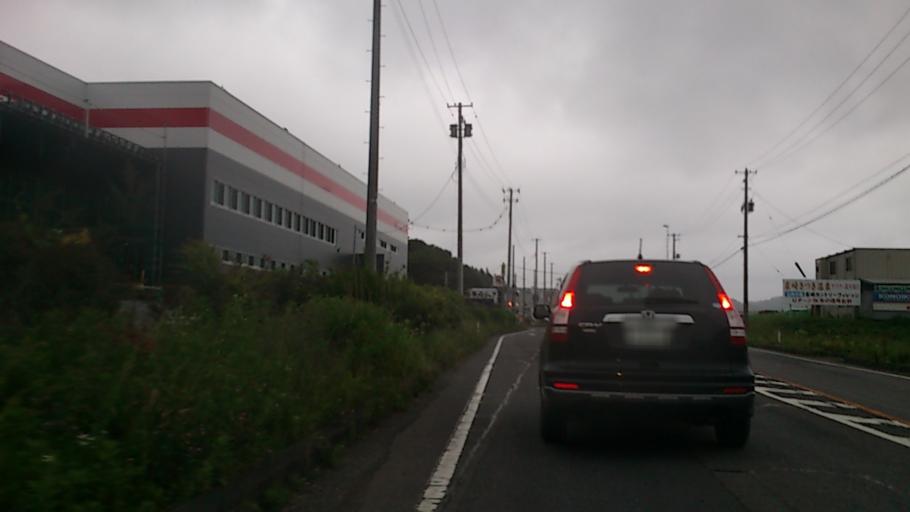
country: JP
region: Fukushima
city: Sukagawa
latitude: 37.1644
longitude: 140.2774
